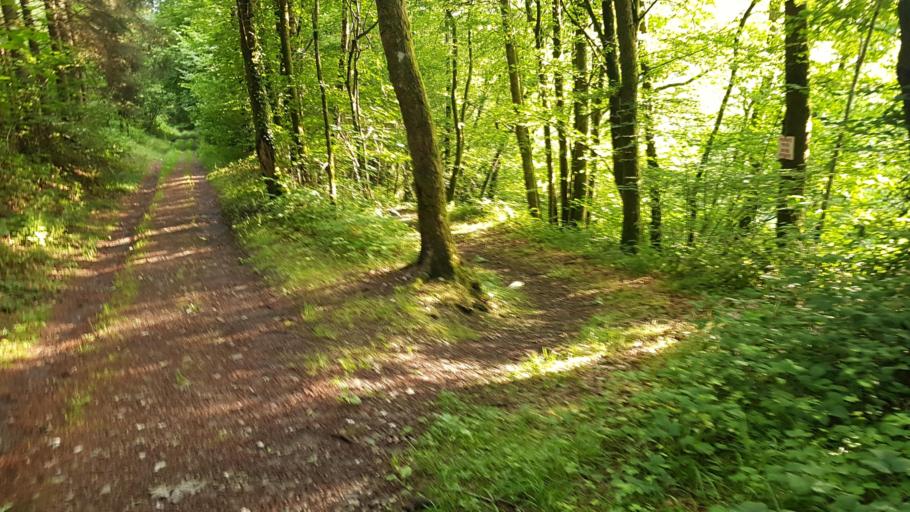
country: BE
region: Wallonia
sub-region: Province du Luxembourg
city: Bouillon
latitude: 49.8007
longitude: 5.0789
